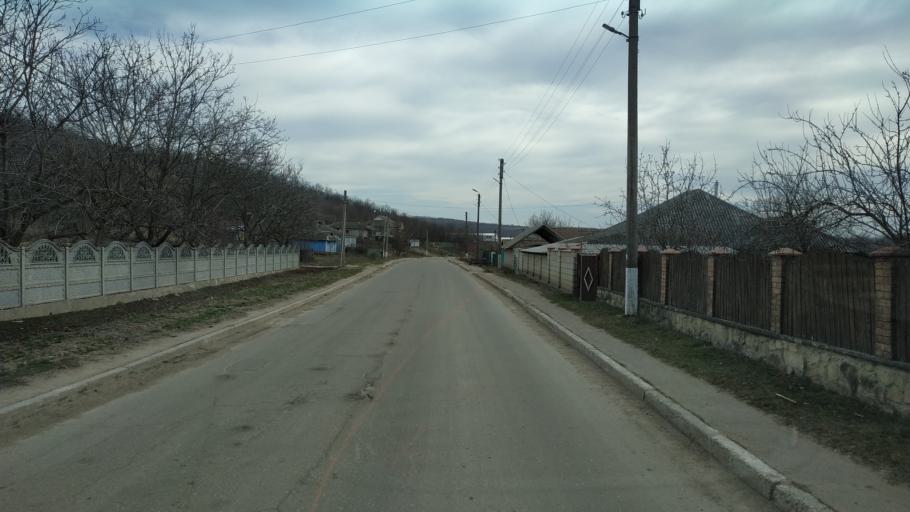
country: MD
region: Nisporeni
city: Nisporeni
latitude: 46.9643
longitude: 28.2154
